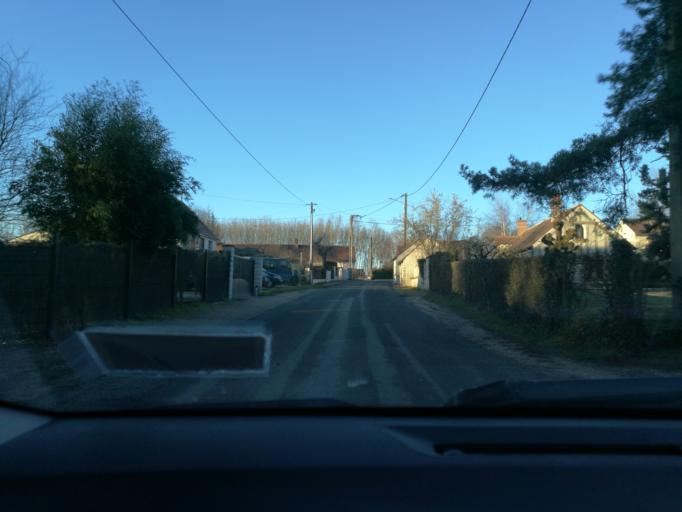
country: FR
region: Centre
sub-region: Departement du Loiret
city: Semoy
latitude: 47.9331
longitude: 1.9657
